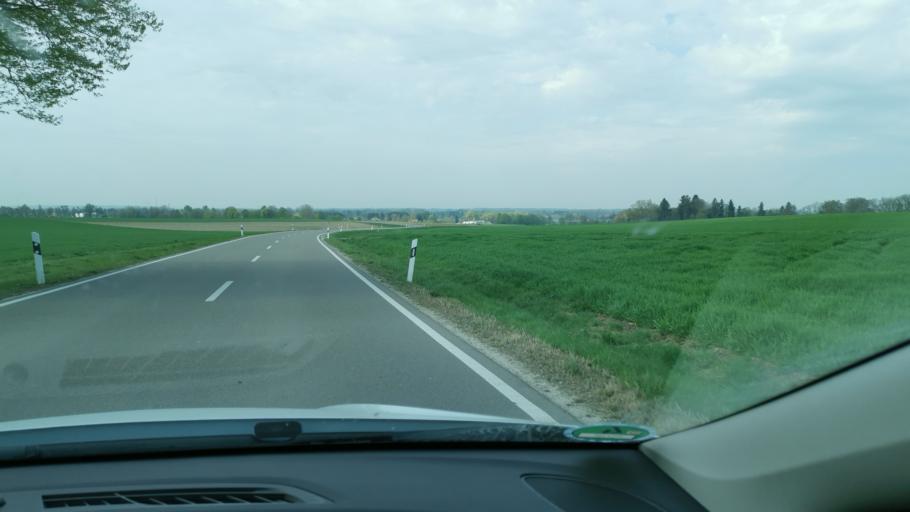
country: DE
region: Bavaria
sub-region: Swabia
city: Thierhaupten
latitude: 48.5802
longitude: 10.9154
